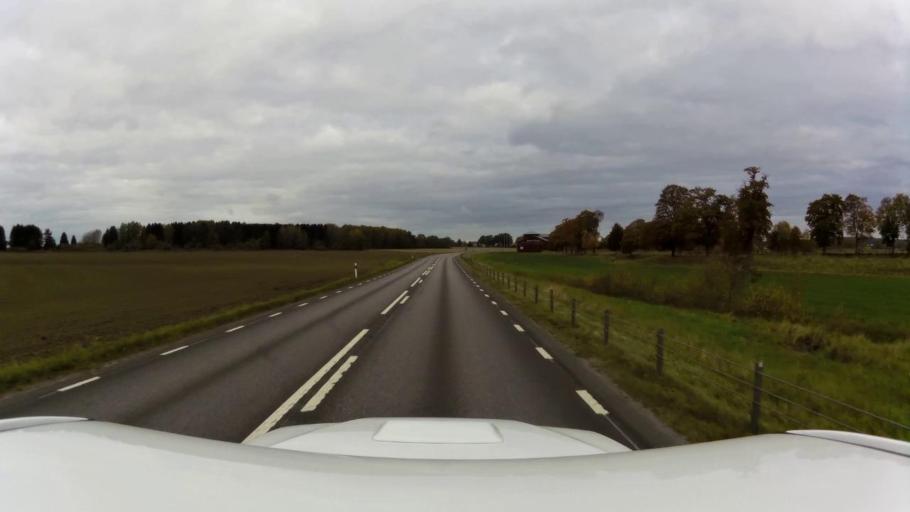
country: SE
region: OEstergoetland
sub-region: Linkopings Kommun
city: Ljungsbro
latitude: 58.5169
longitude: 15.4318
